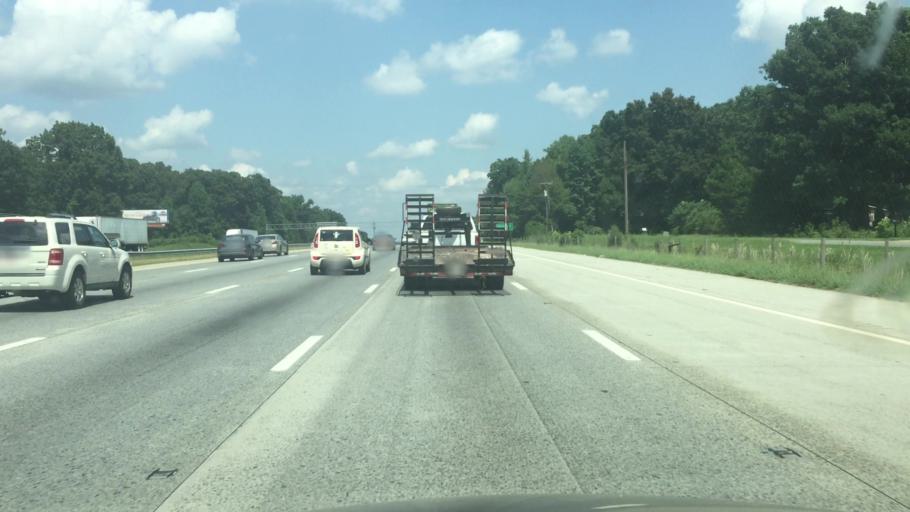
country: US
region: North Carolina
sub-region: Rowan County
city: Salisbury
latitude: 35.6218
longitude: -80.5048
